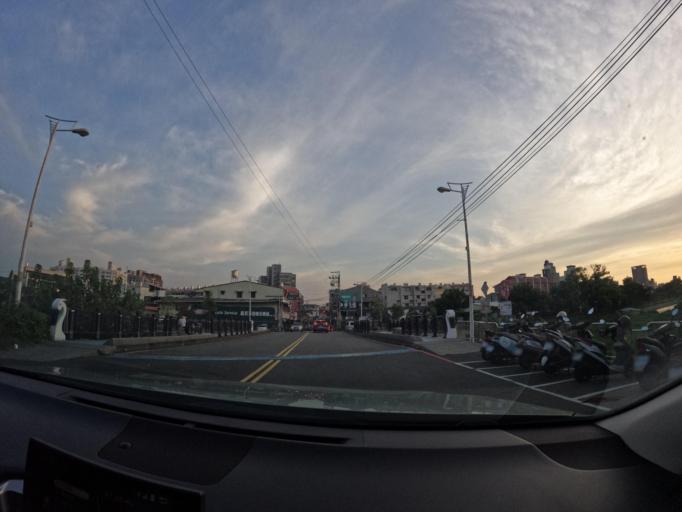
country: TW
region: Taiwan
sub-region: Taichung City
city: Taichung
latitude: 24.1176
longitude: 120.6844
